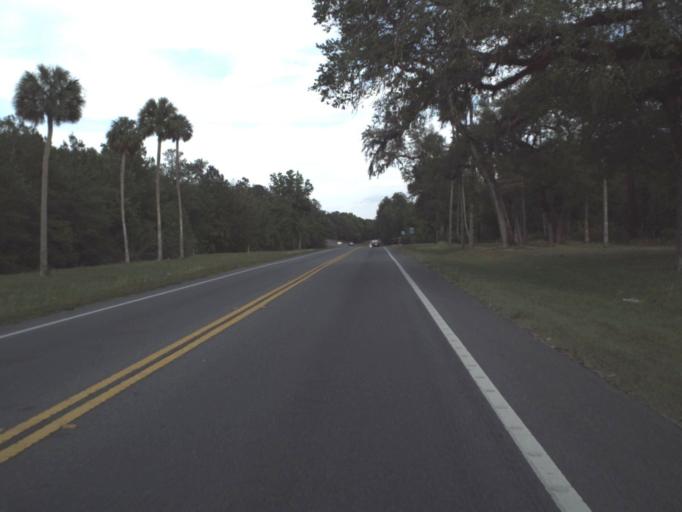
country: US
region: Florida
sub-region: Marion County
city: Silver Springs Shores
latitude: 29.2166
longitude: -82.0015
